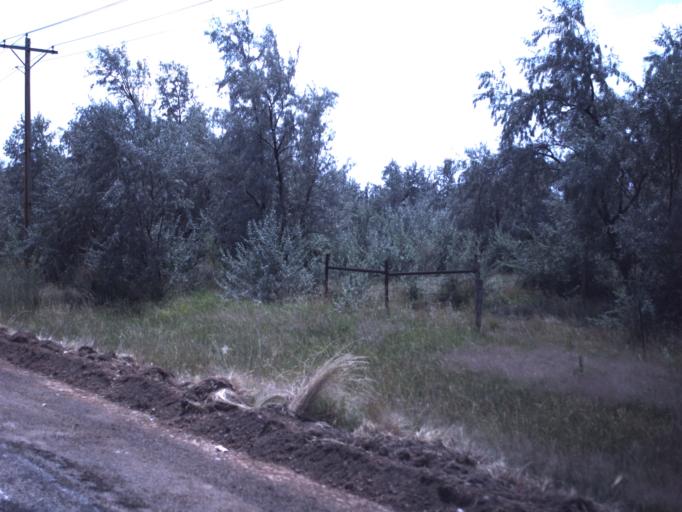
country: US
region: Utah
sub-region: Duchesne County
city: Roosevelt
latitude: 40.3626
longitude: -110.0297
